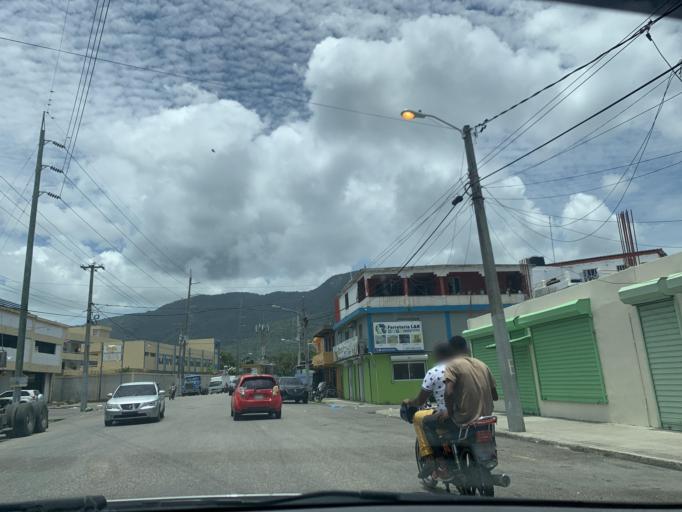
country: DO
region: Puerto Plata
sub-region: Puerto Plata
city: Puerto Plata
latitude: 19.7972
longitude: -70.7019
